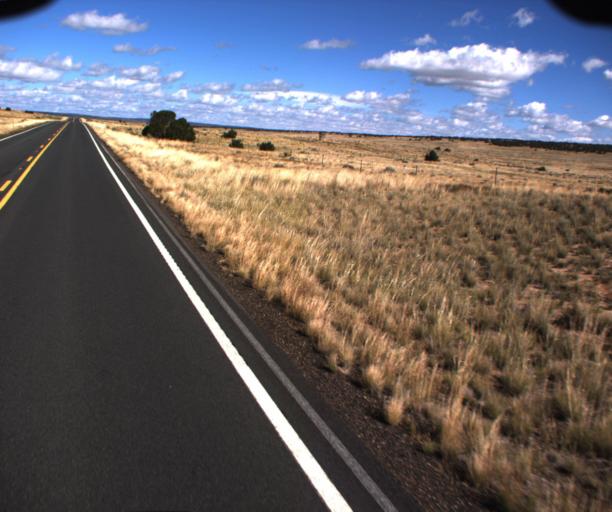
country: US
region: Arizona
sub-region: Apache County
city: Houck
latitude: 34.9688
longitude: -109.2274
